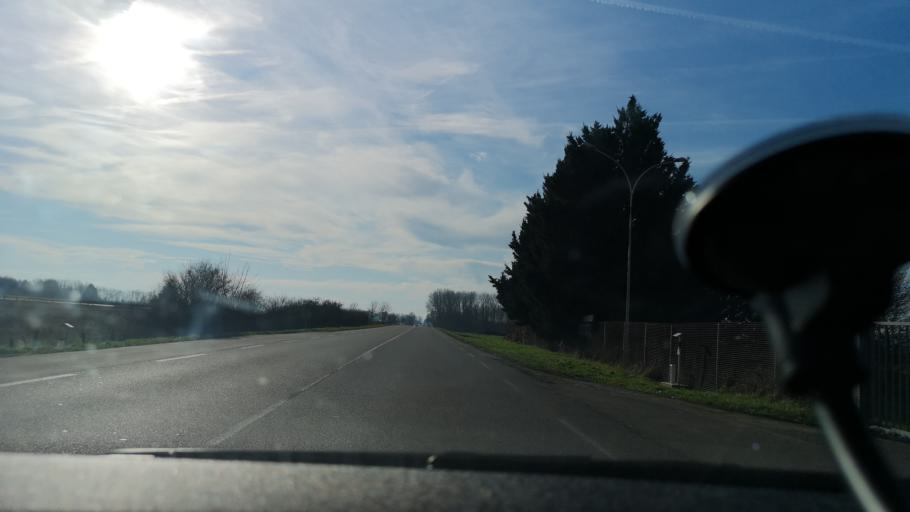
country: FR
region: Bourgogne
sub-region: Departement de Saone-et-Loire
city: Sassenay
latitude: 46.8006
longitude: 4.9357
